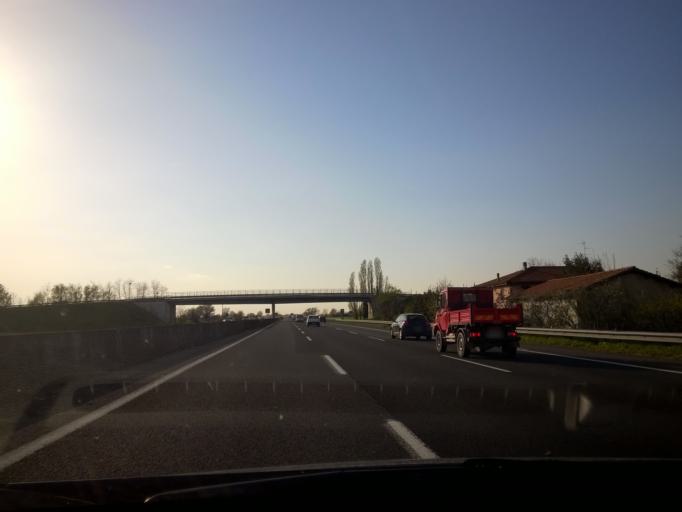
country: IT
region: Emilia-Romagna
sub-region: Provincia di Bologna
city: Castel Guelfo di Bologna
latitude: 44.4086
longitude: 11.6691
